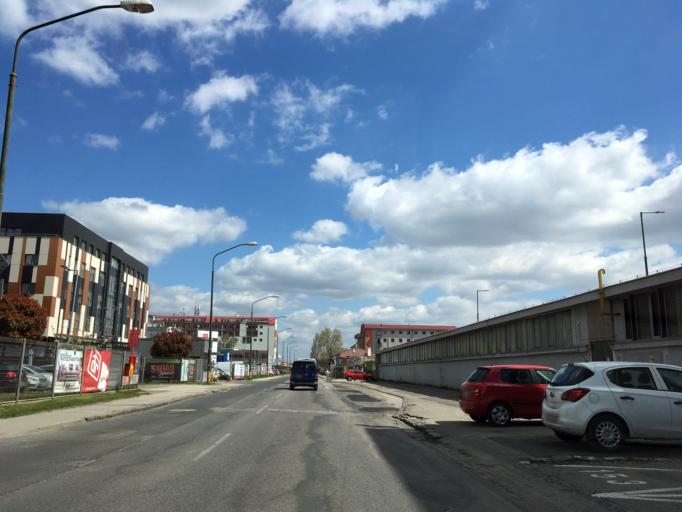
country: SK
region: Bratislavsky
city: Bratislava
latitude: 48.1859
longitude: 17.1649
